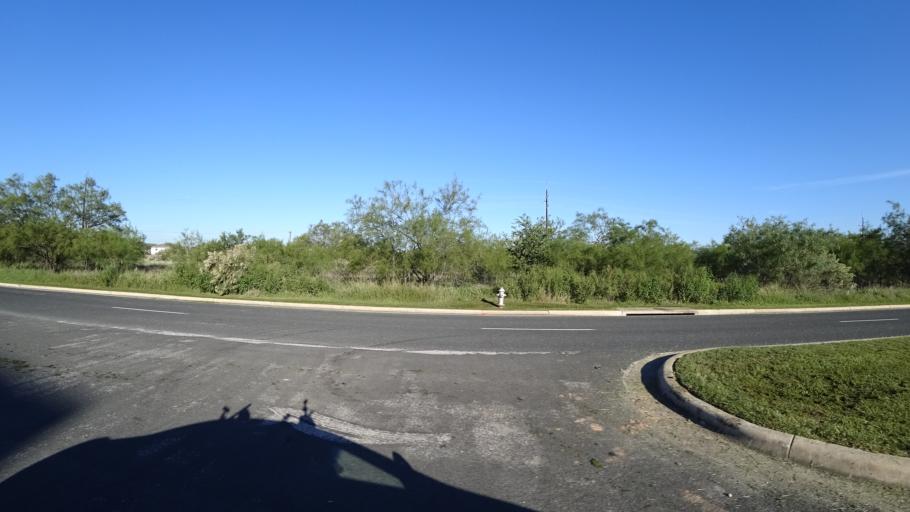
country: US
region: Texas
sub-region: Travis County
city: Austin
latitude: 30.2212
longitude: -97.6906
